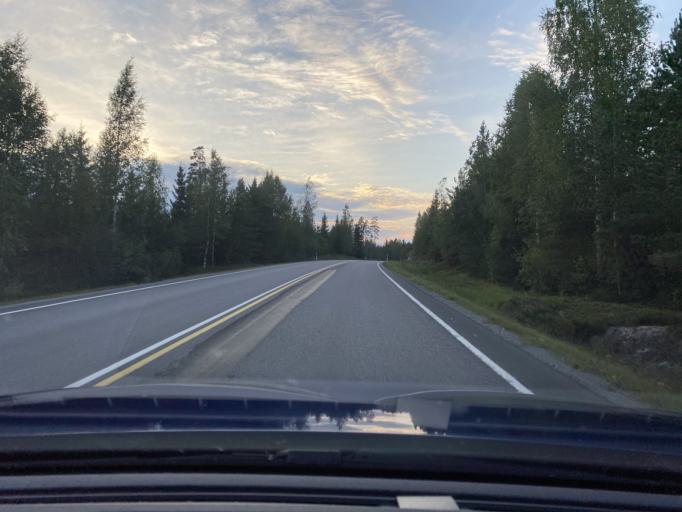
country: FI
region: Satakunta
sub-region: Pohjois-Satakunta
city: Kankaanpaeae
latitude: 61.7738
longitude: 22.4563
